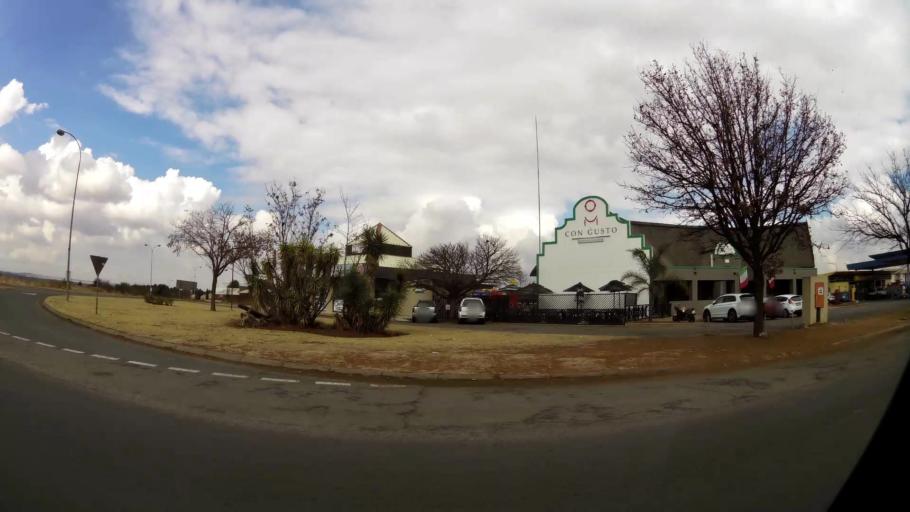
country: ZA
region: Gauteng
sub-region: Sedibeng District Municipality
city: Vanderbijlpark
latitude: -26.7295
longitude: 27.8626
